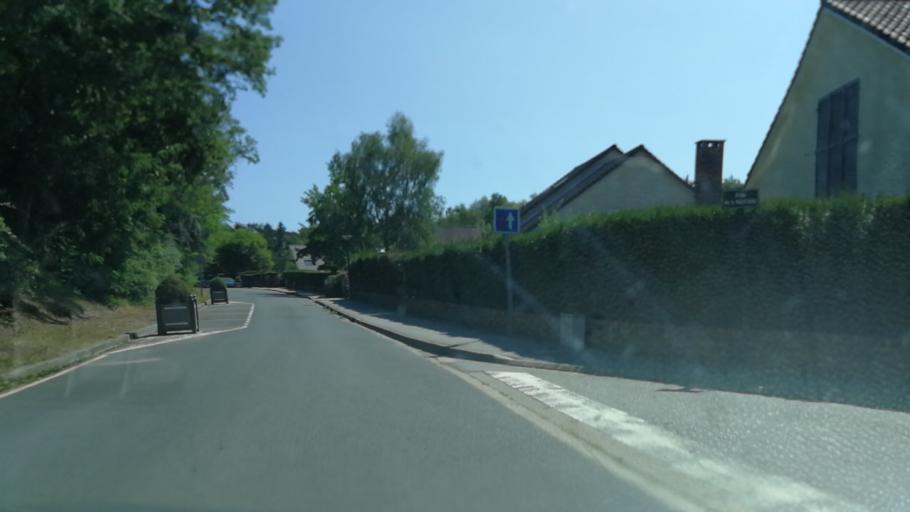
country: FR
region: Ile-de-France
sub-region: Departement des Yvelines
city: Chevreuse
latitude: 48.7056
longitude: 2.0533
